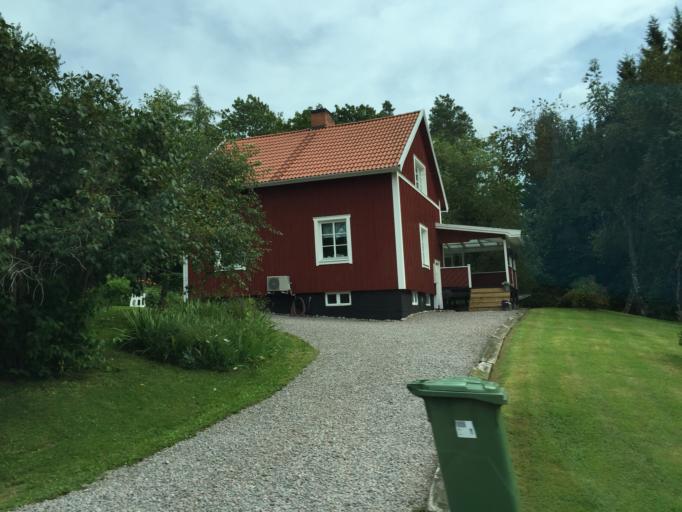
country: SE
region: Uppsala
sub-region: Alvkarleby Kommun
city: AElvkarleby
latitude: 60.4288
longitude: 17.3667
